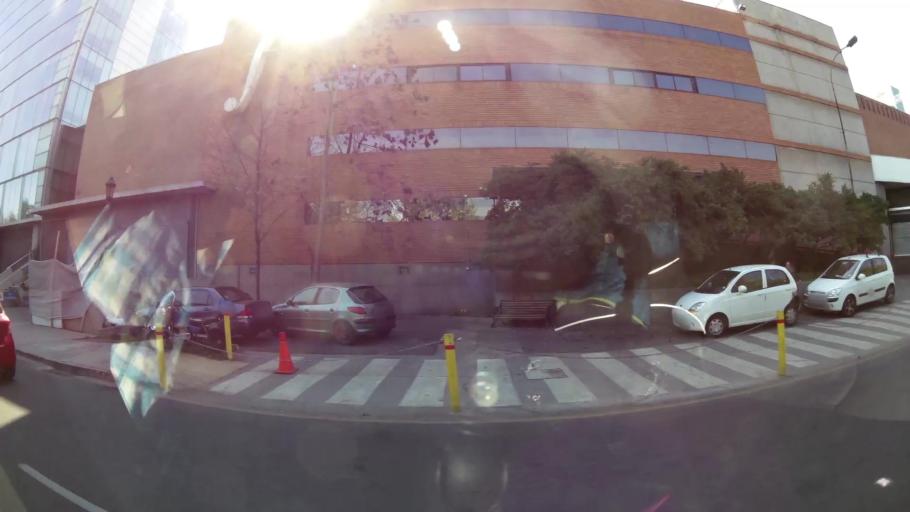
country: CL
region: Santiago Metropolitan
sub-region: Provincia de Santiago
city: Villa Presidente Frei, Nunoa, Santiago, Chile
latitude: -33.4026
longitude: -70.5765
